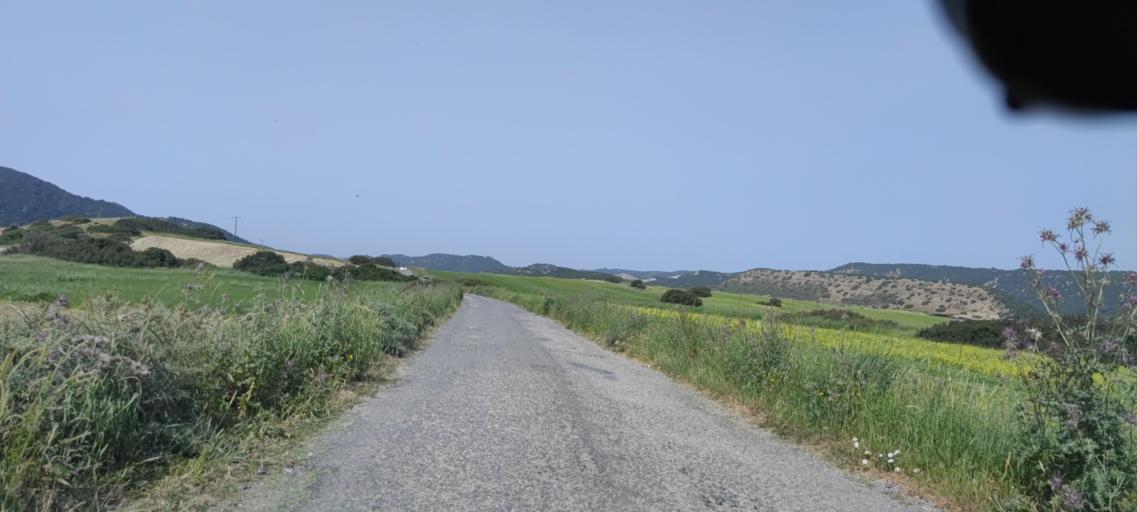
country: CY
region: Ammochostos
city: Rizokarpaso
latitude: 35.6472
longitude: 34.5406
